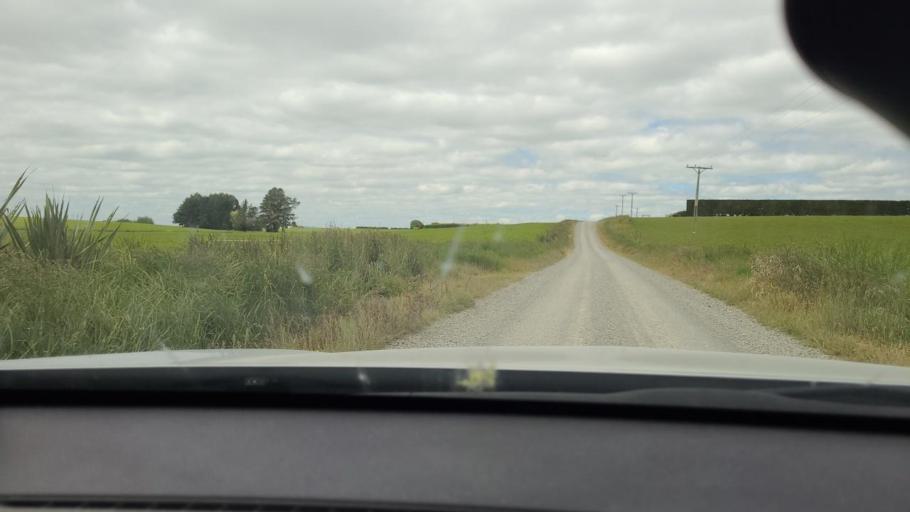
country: NZ
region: Southland
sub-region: Southland District
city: Winton
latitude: -46.2291
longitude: 168.1945
